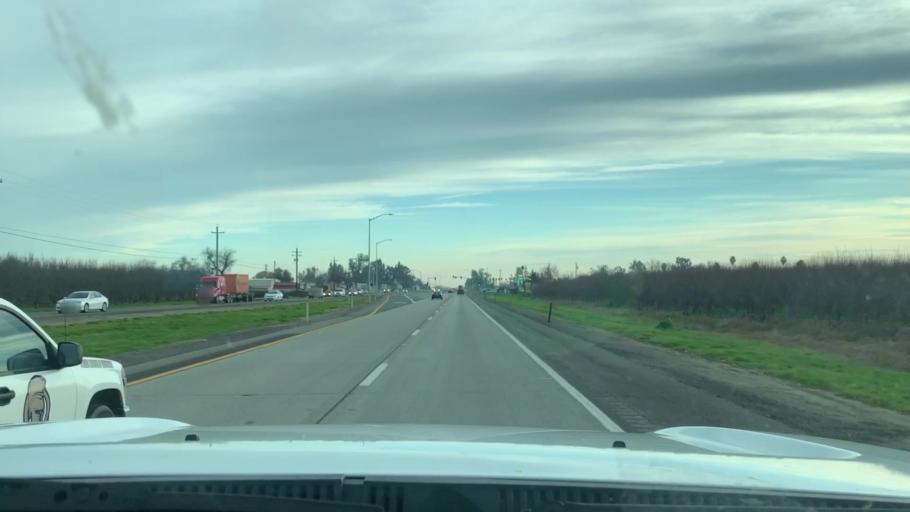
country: US
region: California
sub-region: Kings County
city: Lemoore
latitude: 36.3455
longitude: -119.8083
